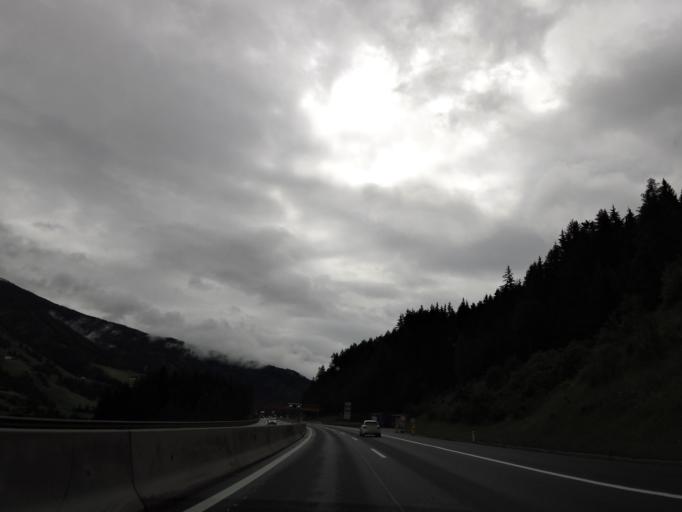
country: AT
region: Tyrol
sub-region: Politischer Bezirk Innsbruck Land
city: Ellbogen
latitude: 47.1611
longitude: 11.4354
